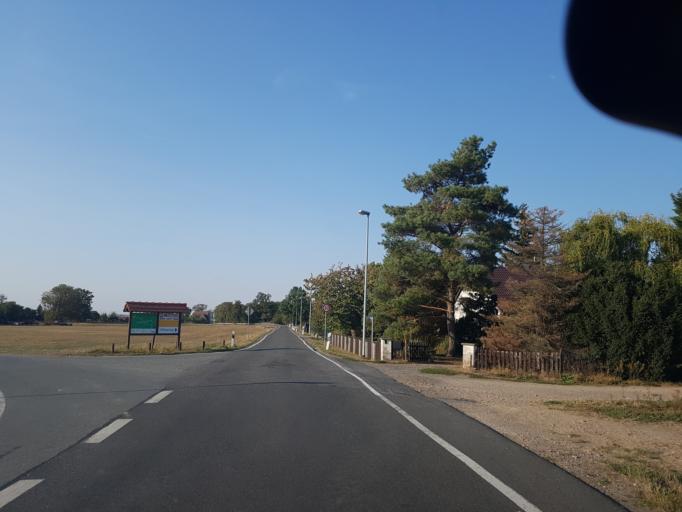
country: DE
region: Saxony
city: Stauchitz
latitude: 51.2866
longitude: 13.1925
